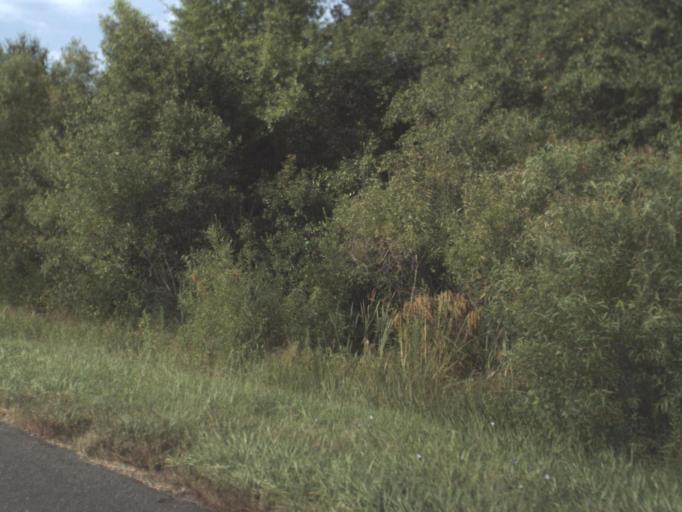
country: US
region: Florida
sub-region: Taylor County
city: Perry
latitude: 30.2629
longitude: -83.6259
